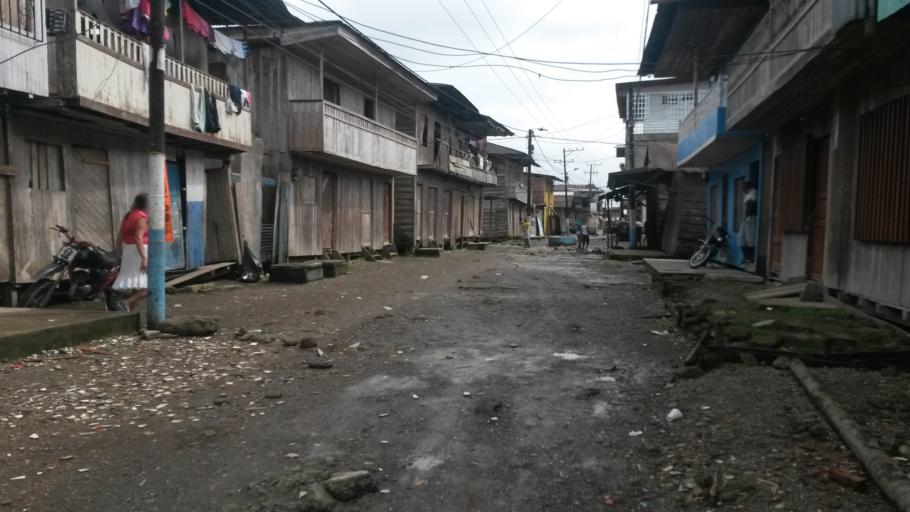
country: CO
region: Cauca
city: Guapi
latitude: 2.5677
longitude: -77.8827
